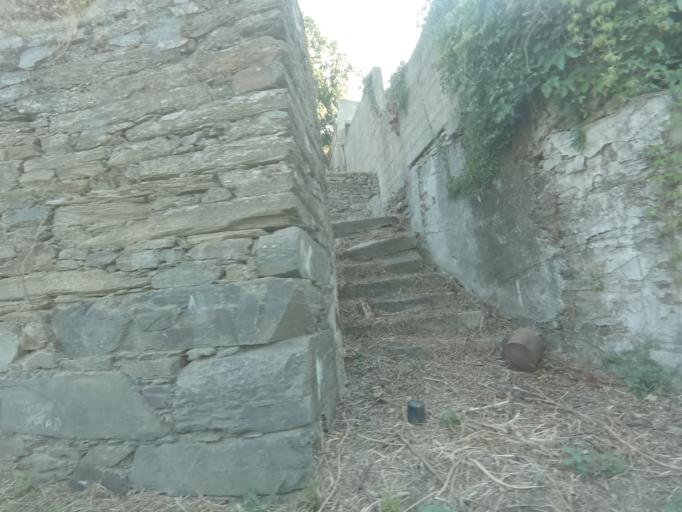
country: PT
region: Vila Real
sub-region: Sabrosa
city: Vilela
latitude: 41.1877
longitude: -7.5921
